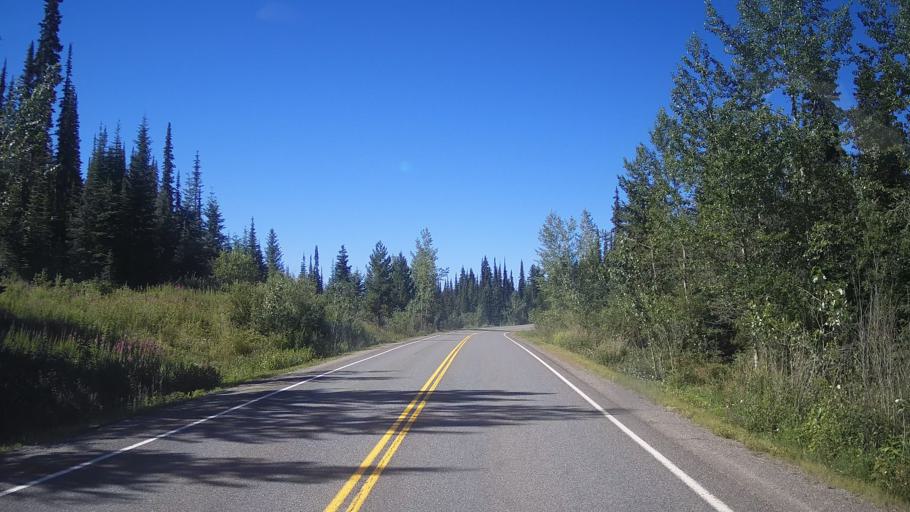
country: CA
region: British Columbia
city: Kamloops
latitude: 51.5007
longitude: -120.3588
